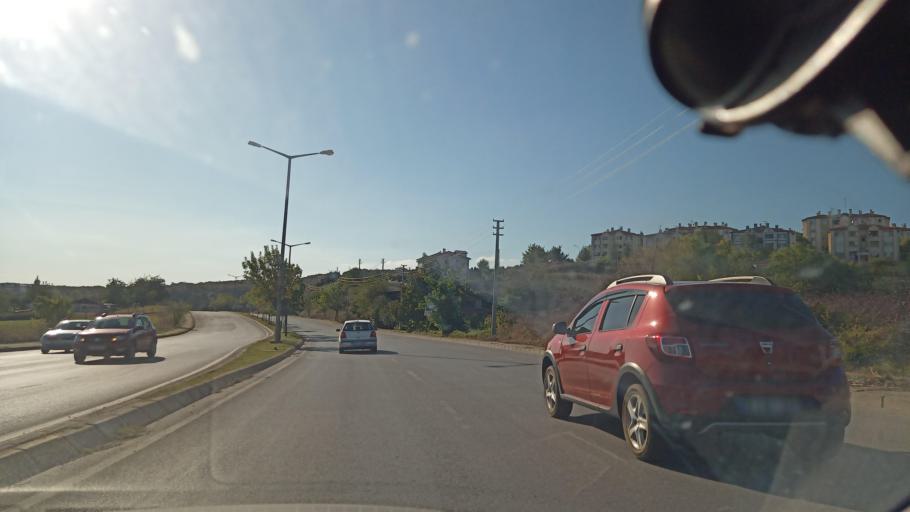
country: TR
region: Sakarya
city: Kazimpasa
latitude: 40.8530
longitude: 30.3068
